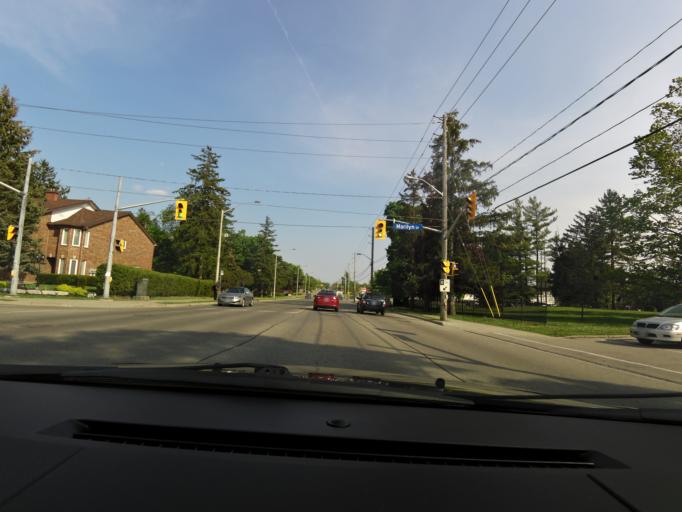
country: CA
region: Ontario
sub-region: Wellington County
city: Guelph
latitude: 43.5621
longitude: -80.2734
